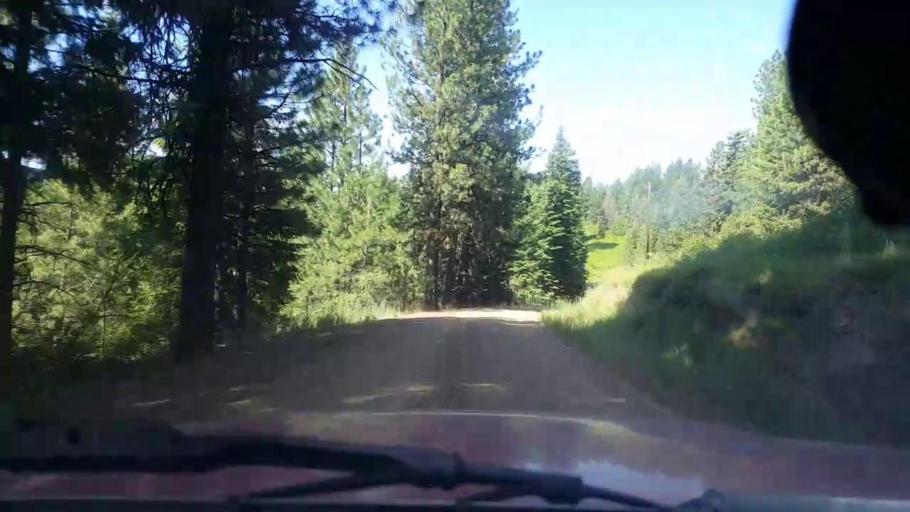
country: US
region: Washington
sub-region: Garfield County
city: Pomeroy
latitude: 46.0353
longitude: -117.4477
